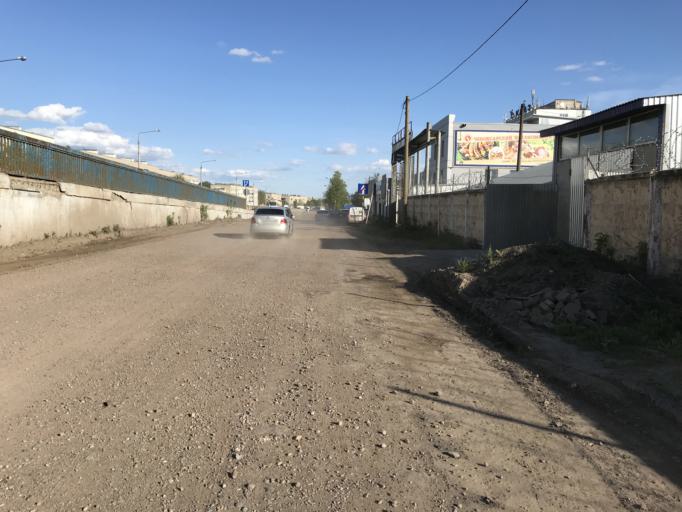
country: RU
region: Chuvashia
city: Kanash
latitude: 55.5032
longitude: 47.4671
